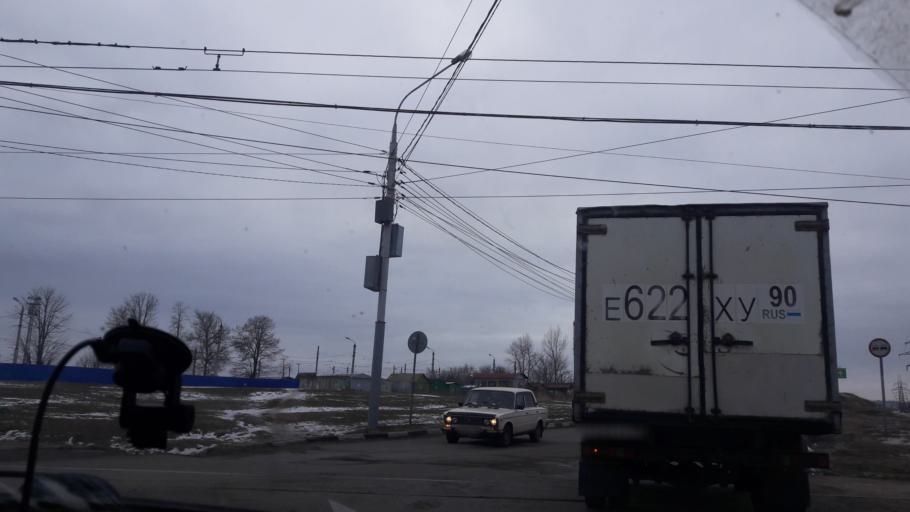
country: RU
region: Tula
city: Tula
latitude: 54.1958
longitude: 37.6605
